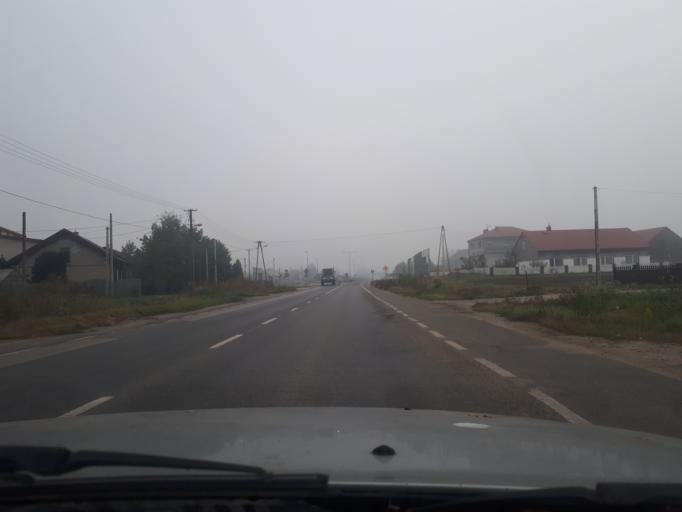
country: PL
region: Lesser Poland Voivodeship
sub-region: Powiat wielicki
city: Niepolomice
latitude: 50.0798
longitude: 20.1793
